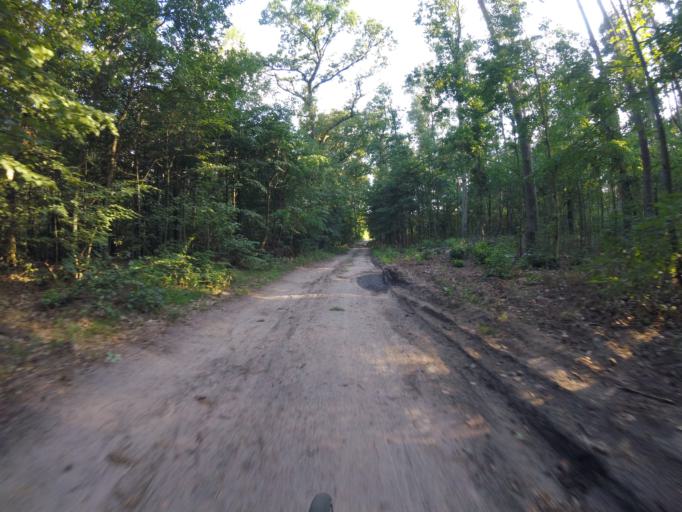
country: DE
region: Brandenburg
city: Petershagen
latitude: 52.5680
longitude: 13.8234
